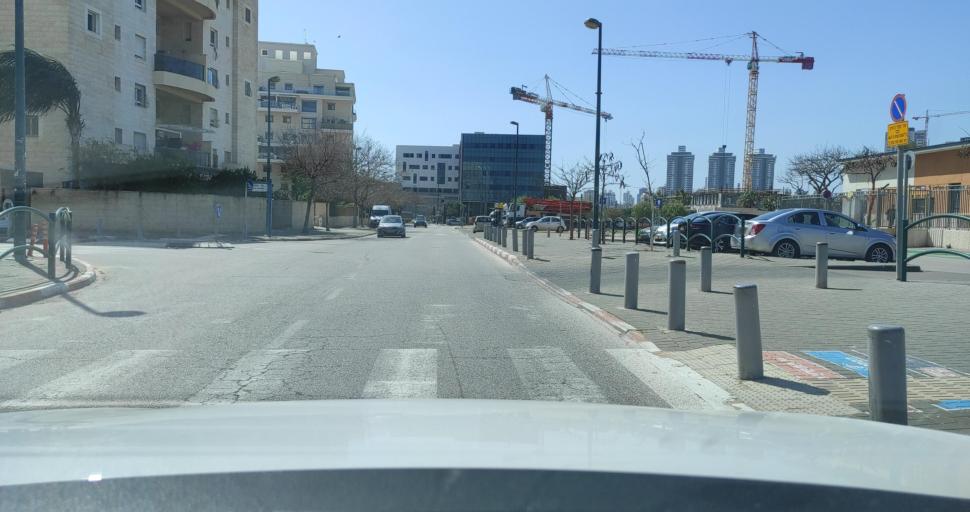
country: IL
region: Central District
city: Bet Yizhaq
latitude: 32.3104
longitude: 34.8718
